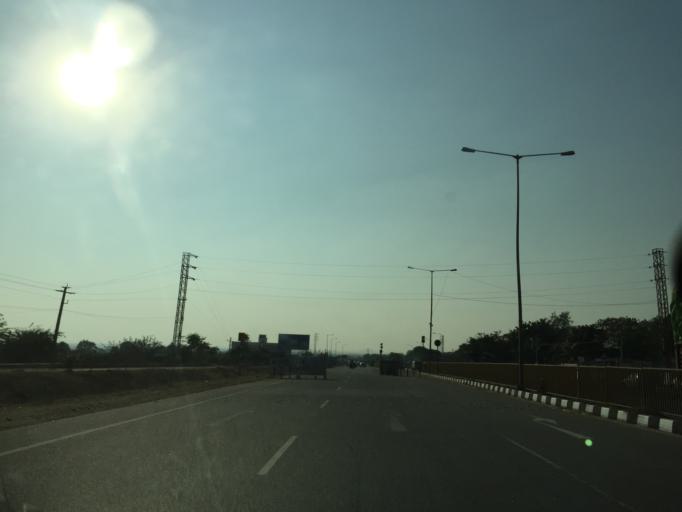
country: IN
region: Telangana
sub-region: Nalgonda
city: Bhongir
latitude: 17.5040
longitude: 78.8608
